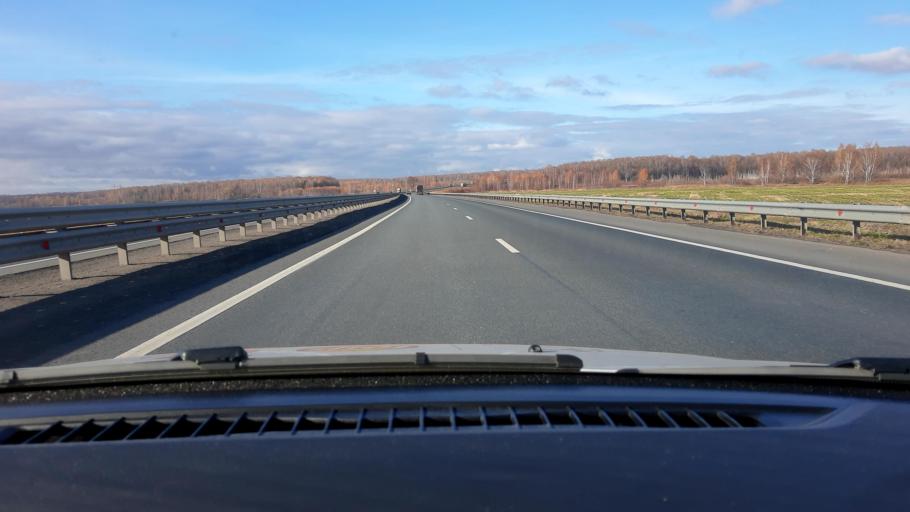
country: RU
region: Nizjnij Novgorod
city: Burevestnik
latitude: 56.1241
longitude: 43.7998
